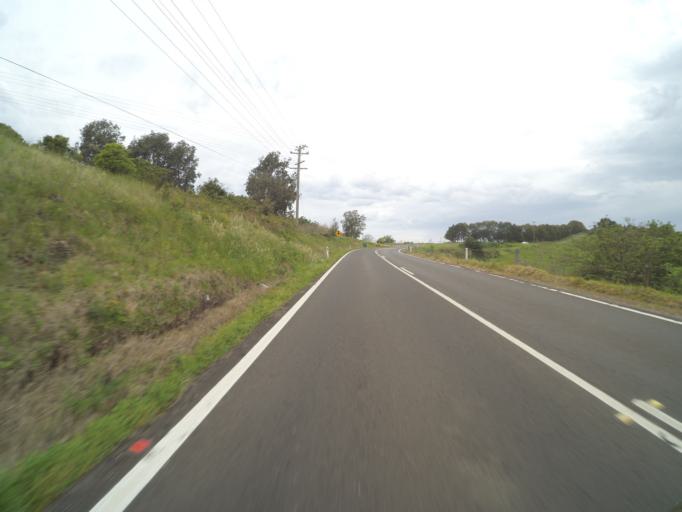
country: AU
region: New South Wales
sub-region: Kiama
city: Kiama
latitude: -34.6661
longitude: 150.8316
